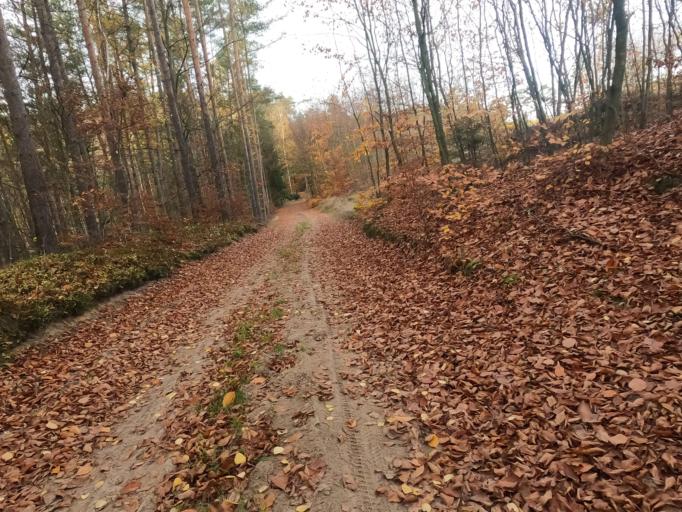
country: PL
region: Pomeranian Voivodeship
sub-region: Powiat starogardzki
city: Skarszewy
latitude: 54.0139
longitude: 18.4630
